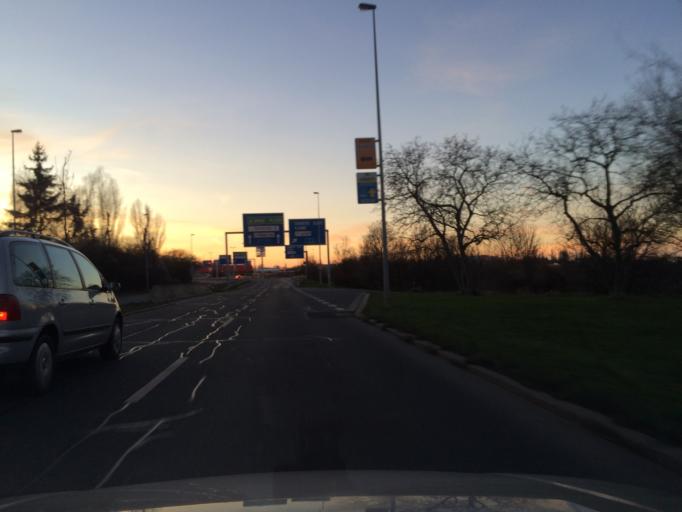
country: CZ
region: Central Bohemia
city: Hostivice
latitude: 50.0937
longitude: 14.3020
